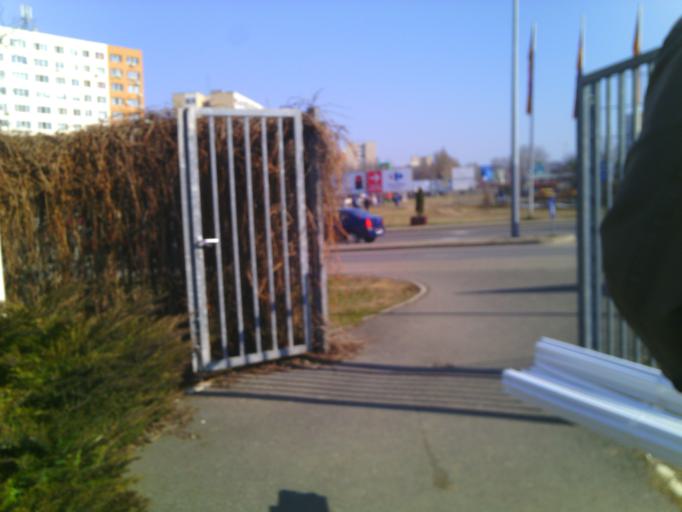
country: RO
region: Ilfov
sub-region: Comuna Popesti-Leordeni
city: Popesti-Leordeni
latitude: 44.3754
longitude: 26.1172
